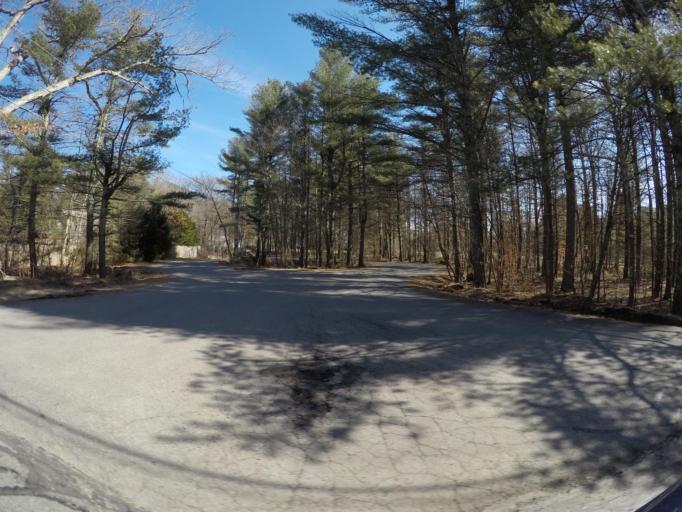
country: US
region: Massachusetts
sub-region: Bristol County
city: Easton
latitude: 42.0723
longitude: -71.1385
